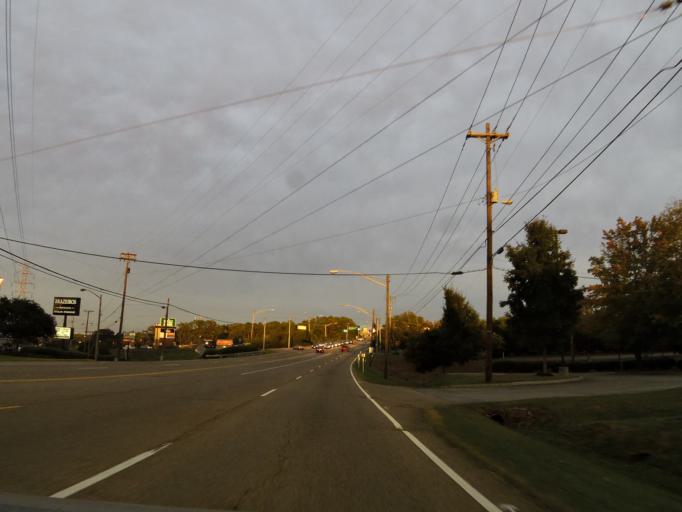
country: US
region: Tennessee
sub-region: Knox County
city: Knoxville
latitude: 35.9325
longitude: -84.0192
